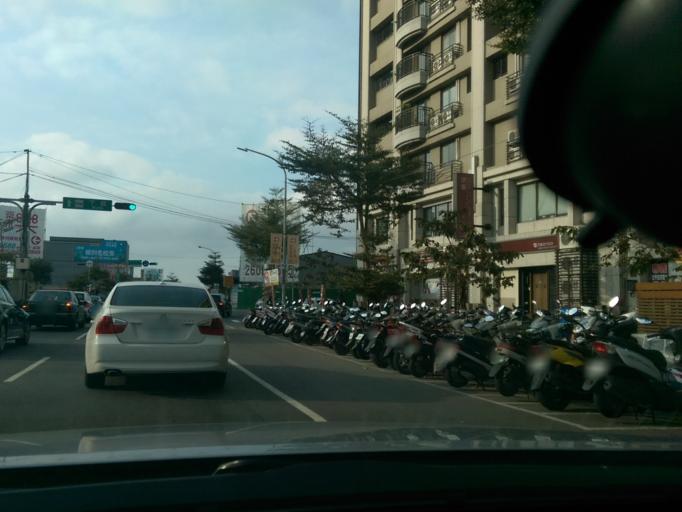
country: TW
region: Taiwan
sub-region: Taoyuan
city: Taoyuan
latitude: 25.0839
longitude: 121.3779
